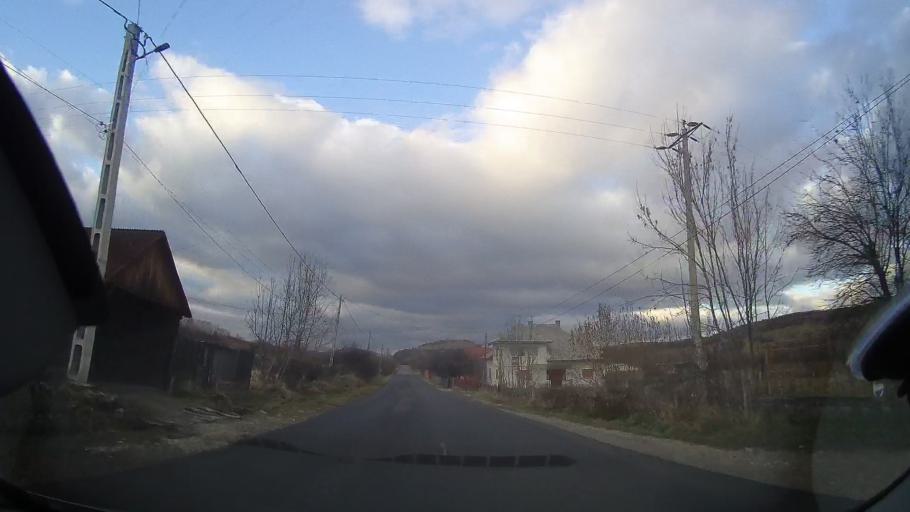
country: RO
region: Cluj
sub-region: Comuna Calatele
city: Calatele
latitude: 46.7761
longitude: 23.0068
